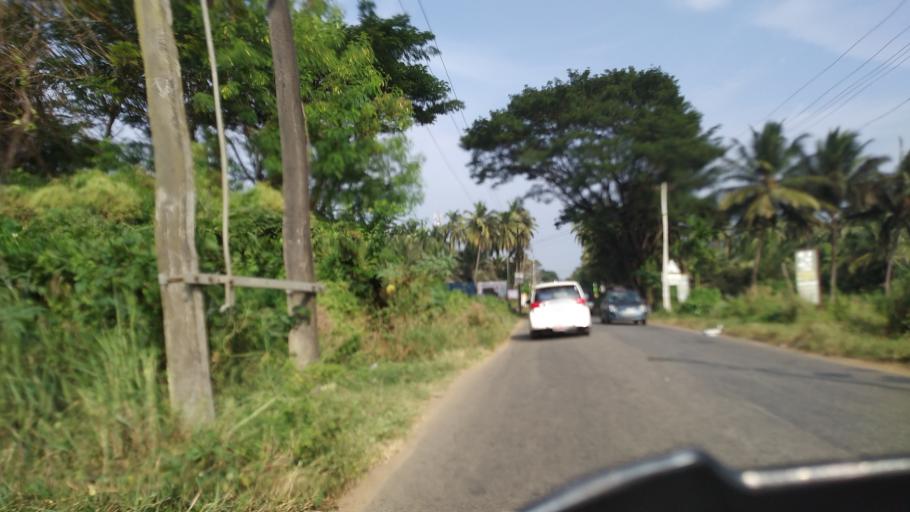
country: IN
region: Kerala
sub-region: Thrissur District
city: Chelakara
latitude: 10.5879
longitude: 76.5098
